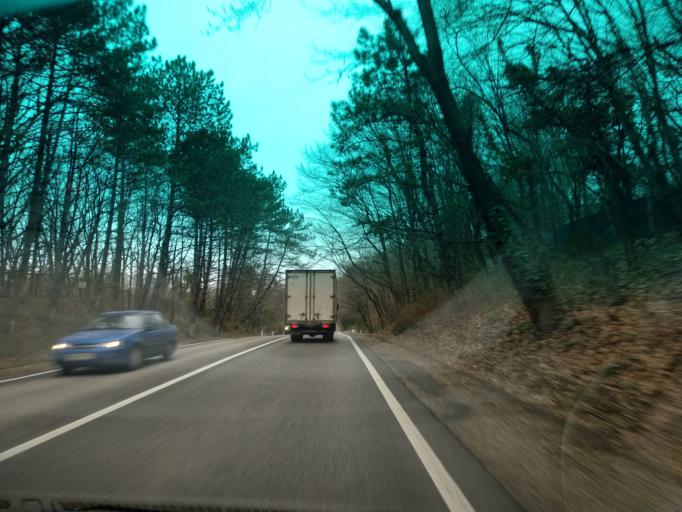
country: RU
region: Krasnodarskiy
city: Agoy
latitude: 44.1469
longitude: 39.0185
